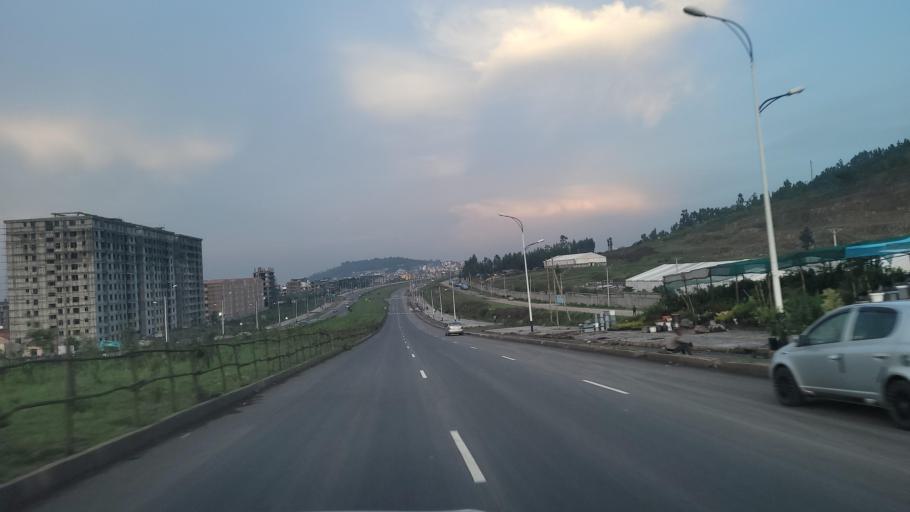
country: ET
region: Adis Abeba
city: Addis Ababa
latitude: 8.9494
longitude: 38.7073
